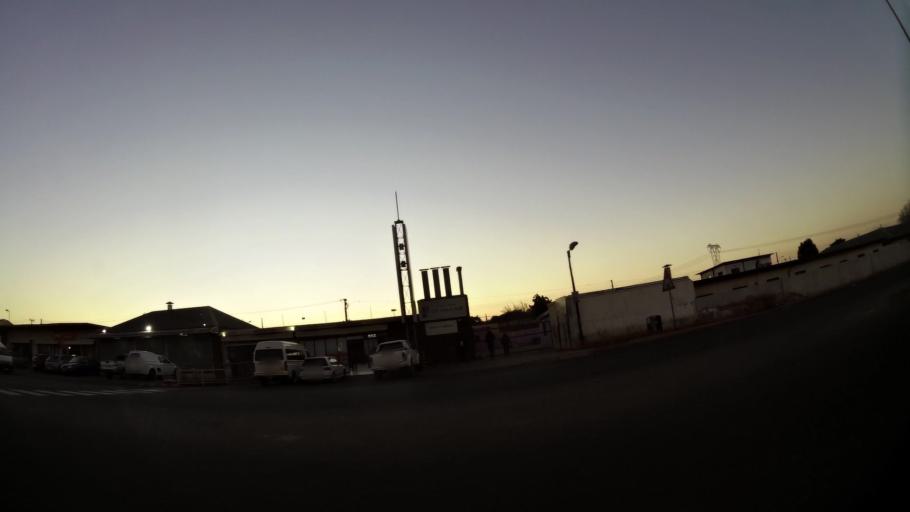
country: ZA
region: North-West
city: Ga-Rankuwa
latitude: -25.5880
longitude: 27.9863
